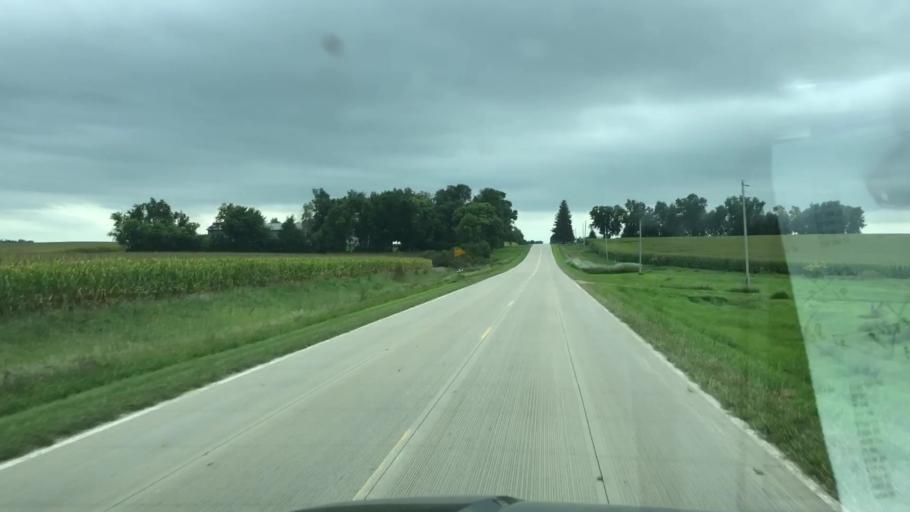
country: US
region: Iowa
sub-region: Sioux County
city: Alton
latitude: 43.1124
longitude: -95.9787
